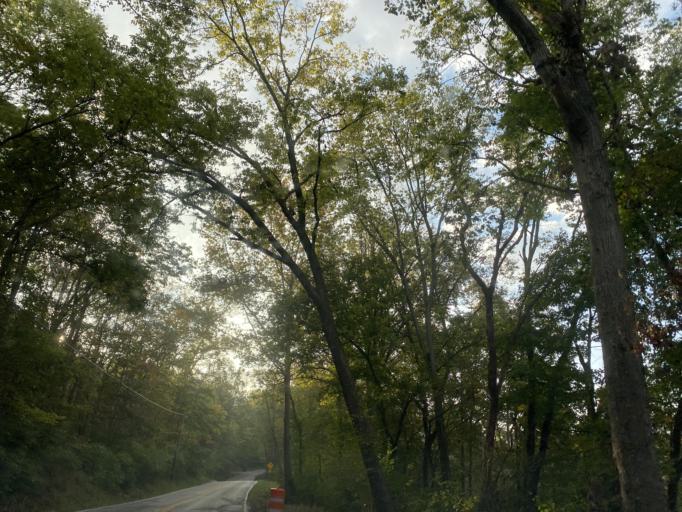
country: US
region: Kentucky
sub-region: Pendleton County
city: Falmouth
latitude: 38.7888
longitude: -84.3379
